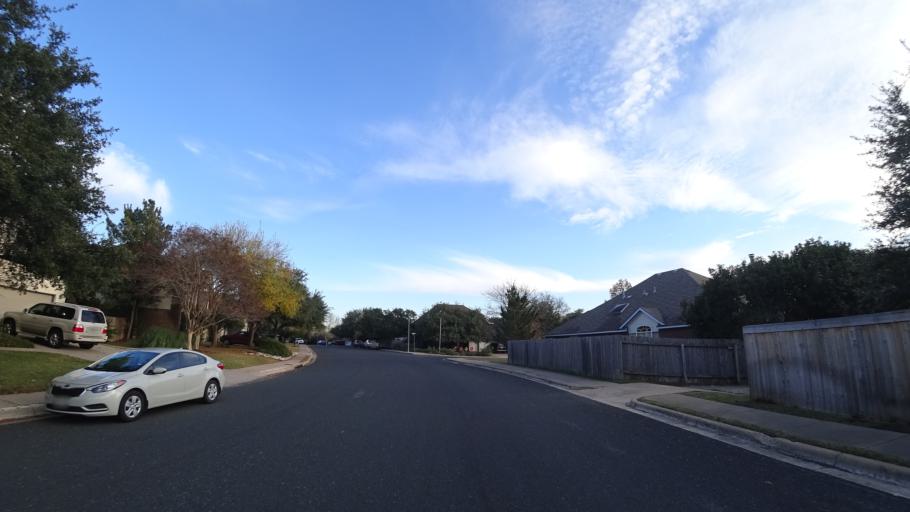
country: US
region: Texas
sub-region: Williamson County
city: Brushy Creek
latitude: 30.4884
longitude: -97.7373
